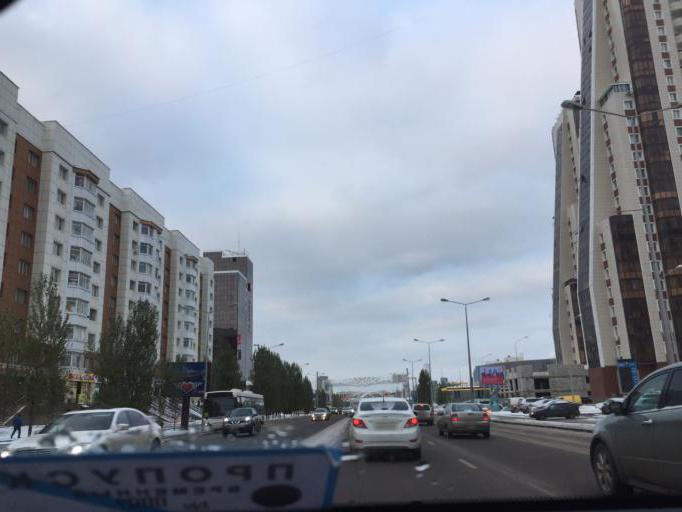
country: KZ
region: Astana Qalasy
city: Astana
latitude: 51.1381
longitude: 71.4711
